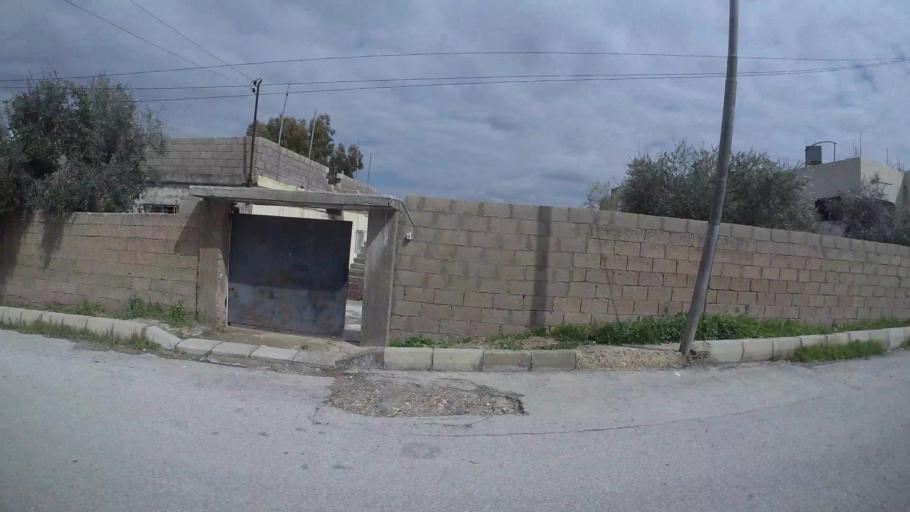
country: JO
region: Amman
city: Al Jubayhah
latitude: 32.0524
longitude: 35.8277
